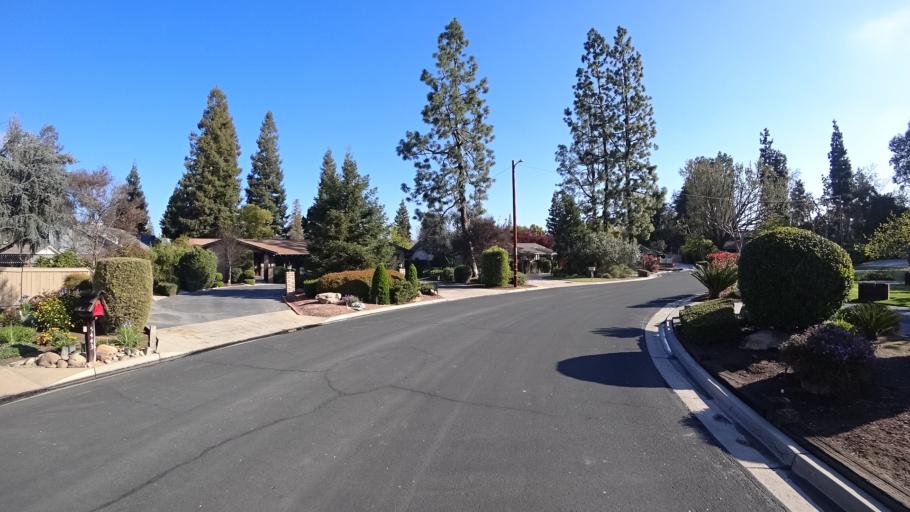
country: US
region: California
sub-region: Fresno County
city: Fresno
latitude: 36.8163
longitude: -119.8252
